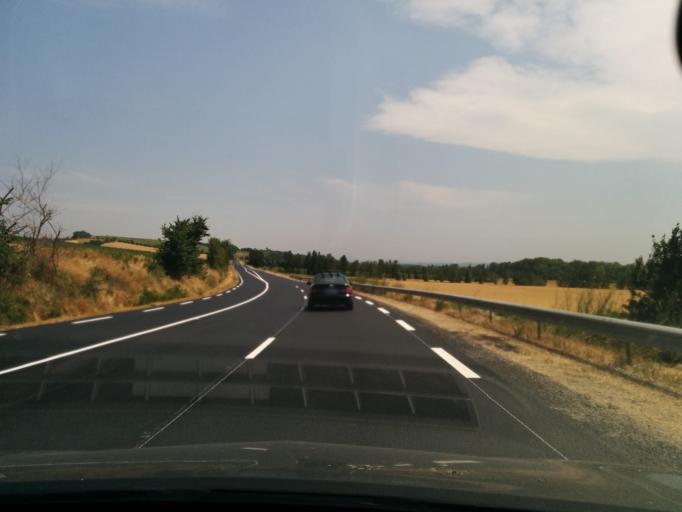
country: FR
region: Languedoc-Roussillon
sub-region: Departement de l'Aude
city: Villepinte
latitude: 43.2755
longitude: 2.1004
